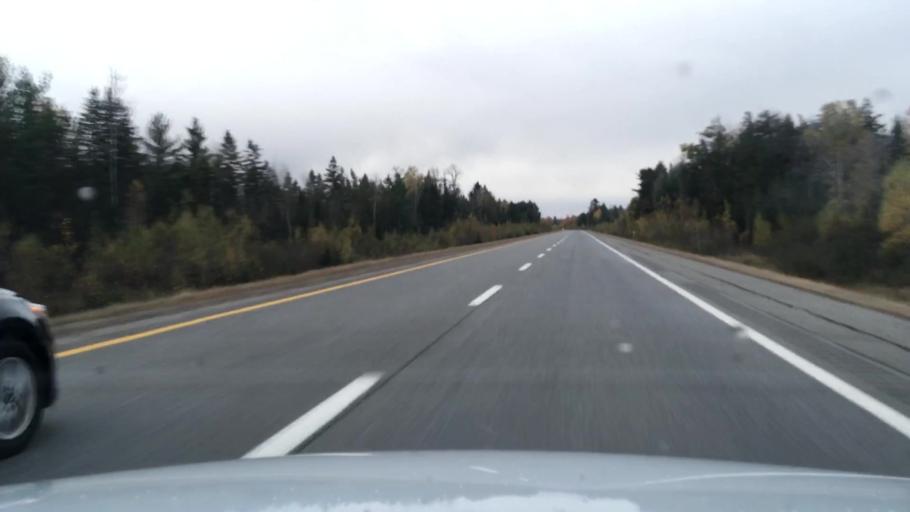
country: US
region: Maine
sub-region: Penobscot County
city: Greenbush
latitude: 45.1075
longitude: -68.6957
